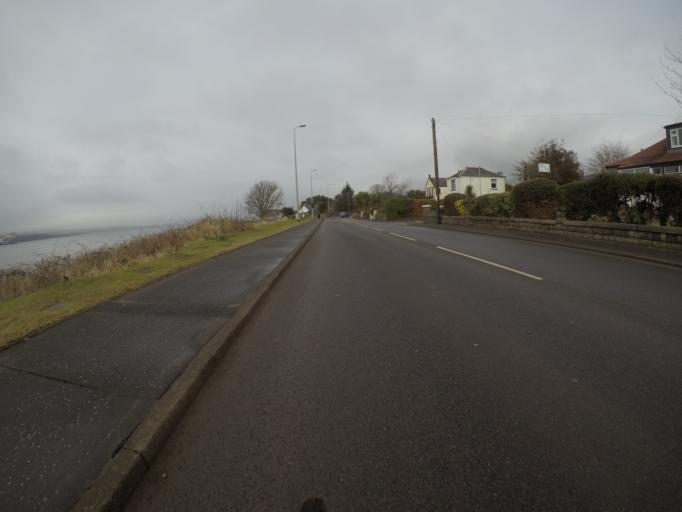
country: GB
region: Scotland
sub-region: North Ayrshire
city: Fairlie
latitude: 55.7495
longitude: -4.8570
